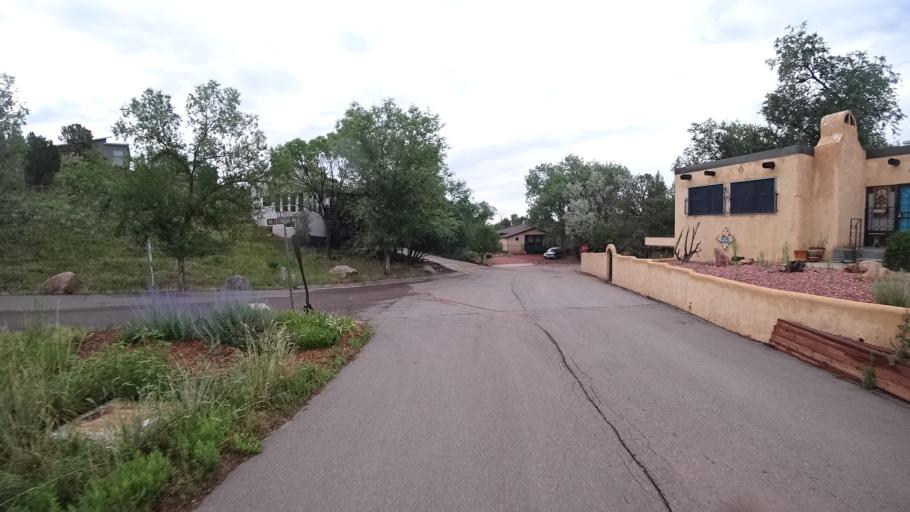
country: US
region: Colorado
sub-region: El Paso County
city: Manitou Springs
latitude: 38.8610
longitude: -104.8944
